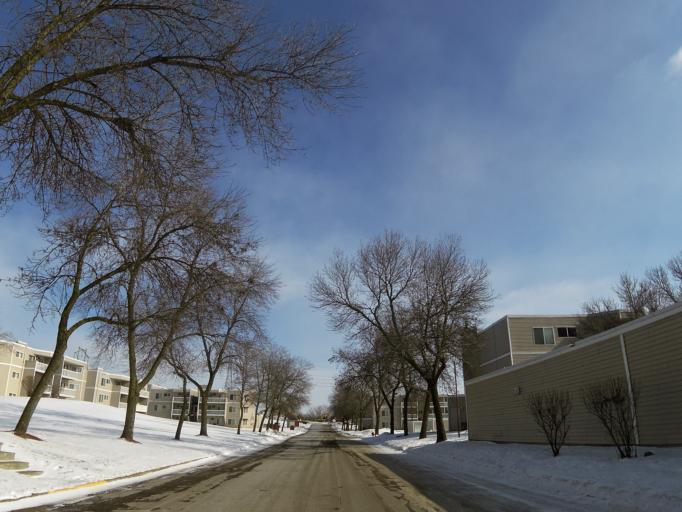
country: US
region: Minnesota
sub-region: Washington County
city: Oakdale
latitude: 44.9472
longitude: -92.9674
